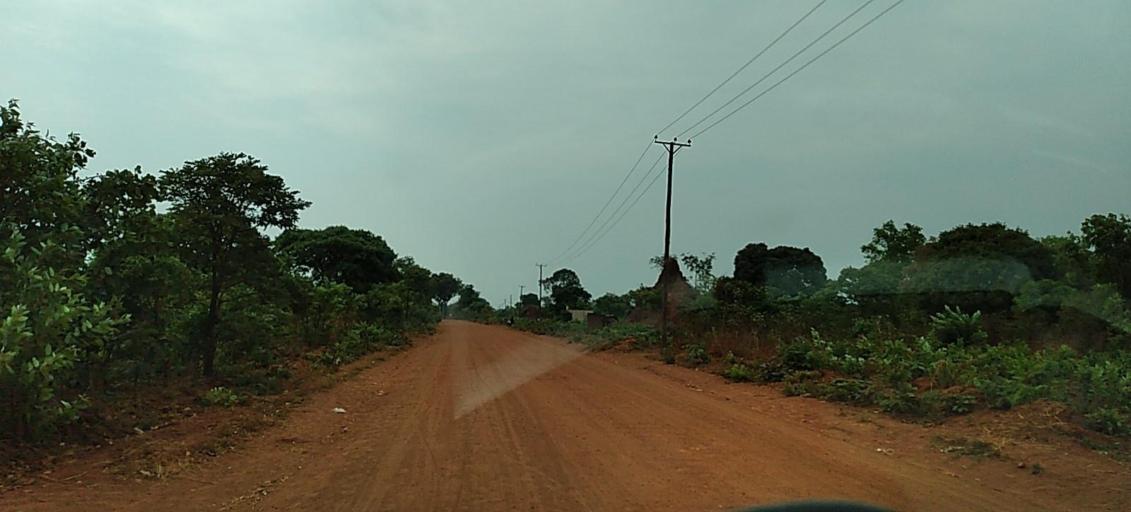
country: ZM
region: North-Western
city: Solwezi
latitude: -12.2037
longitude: 26.4953
